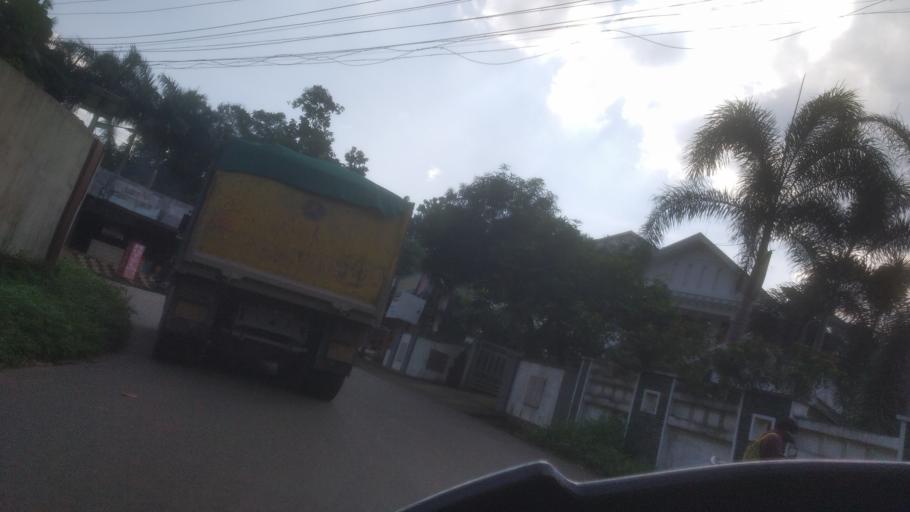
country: IN
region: Kerala
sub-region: Ernakulam
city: Kotamangalam
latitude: 10.0062
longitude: 76.6785
